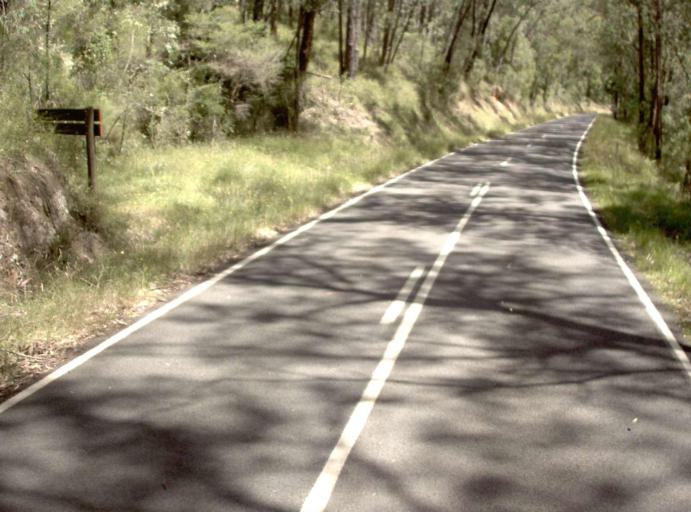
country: AU
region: Victoria
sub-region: Baw Baw
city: Warragul
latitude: -37.8960
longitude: 146.0276
